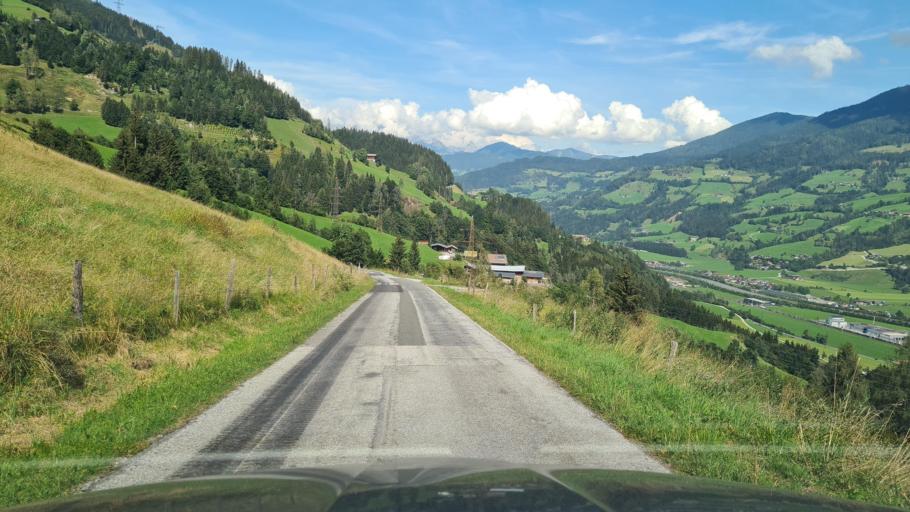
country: AT
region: Salzburg
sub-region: Politischer Bezirk Sankt Johann im Pongau
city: Sankt Johann im Pongau
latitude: 47.3563
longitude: 13.1868
